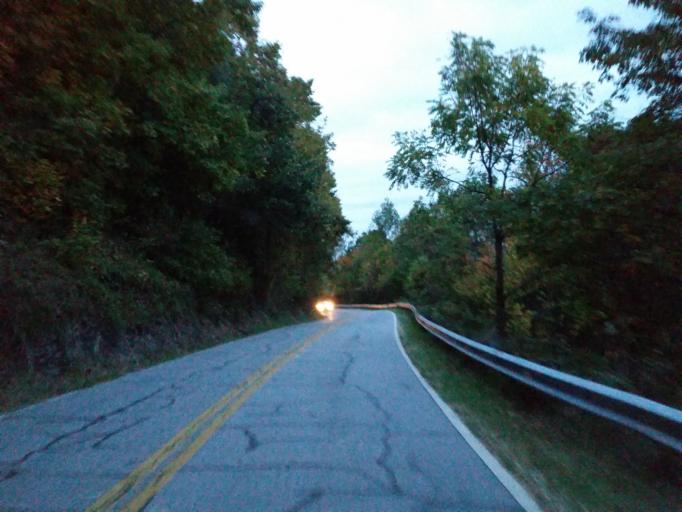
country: US
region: Georgia
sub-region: Lumpkin County
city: Dahlonega
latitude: 34.6485
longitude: -83.9682
